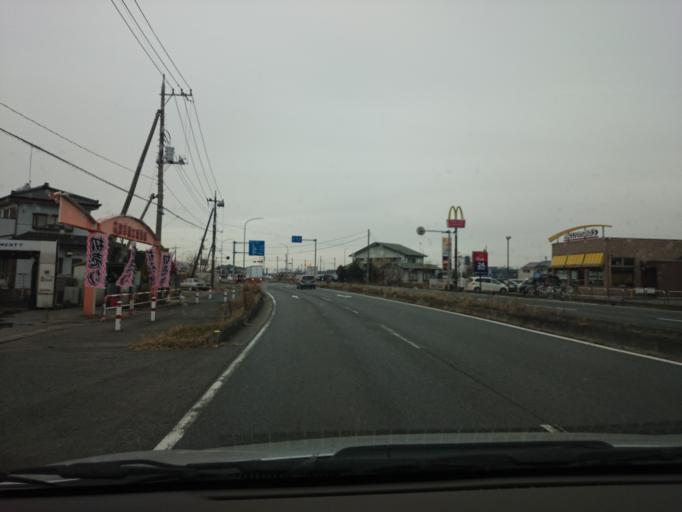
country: JP
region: Saitama
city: Hanyu
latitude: 36.1419
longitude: 139.5554
